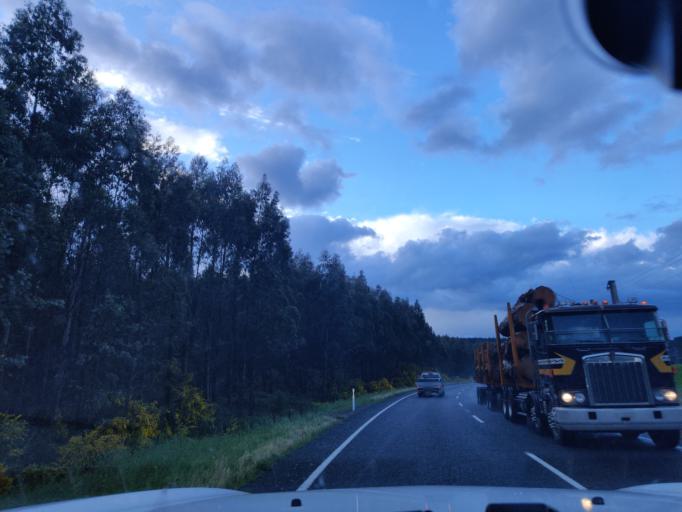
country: NZ
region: Waikato
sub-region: South Waikato District
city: Tokoroa
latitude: -38.3613
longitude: 175.8067
